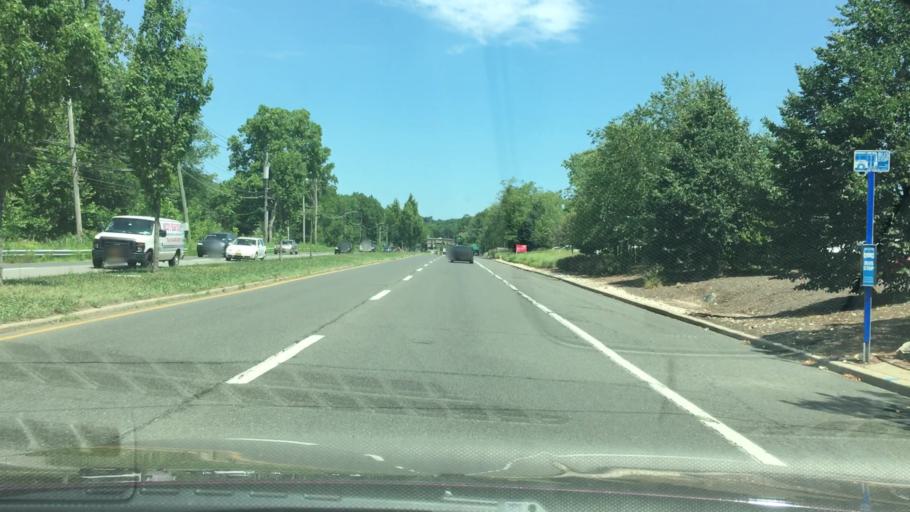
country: US
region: New York
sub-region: Westchester County
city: Mamaroneck
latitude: 40.9793
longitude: -73.7434
